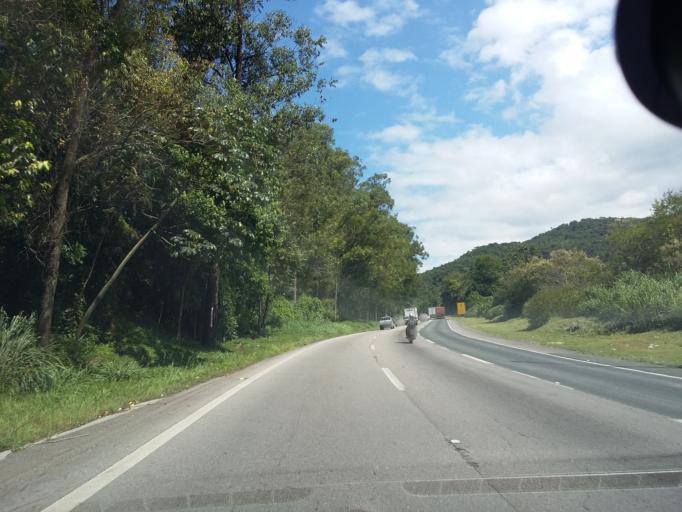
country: BR
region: Santa Catarina
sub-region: Balneario Camboriu
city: Balneario Camboriu
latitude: -27.0322
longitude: -48.6005
